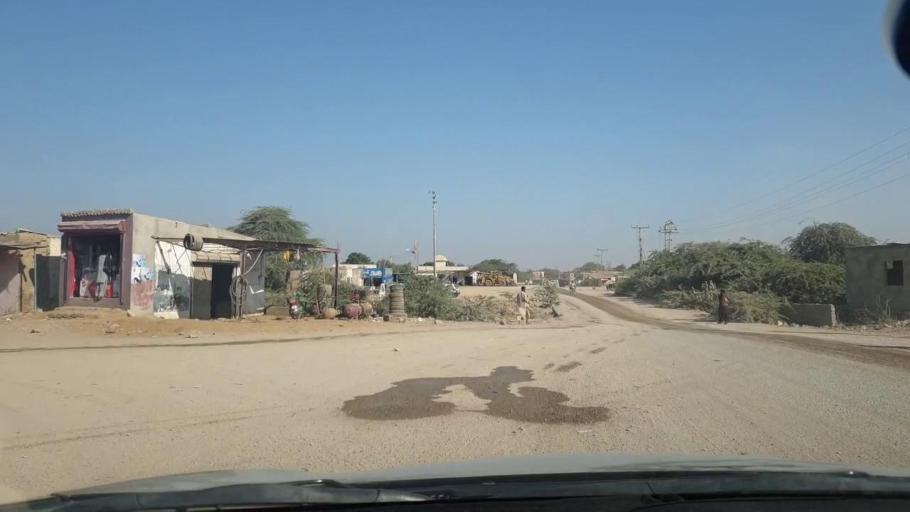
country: PK
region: Sindh
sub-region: Karachi District
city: Karachi
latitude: 25.0912
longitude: 67.0134
